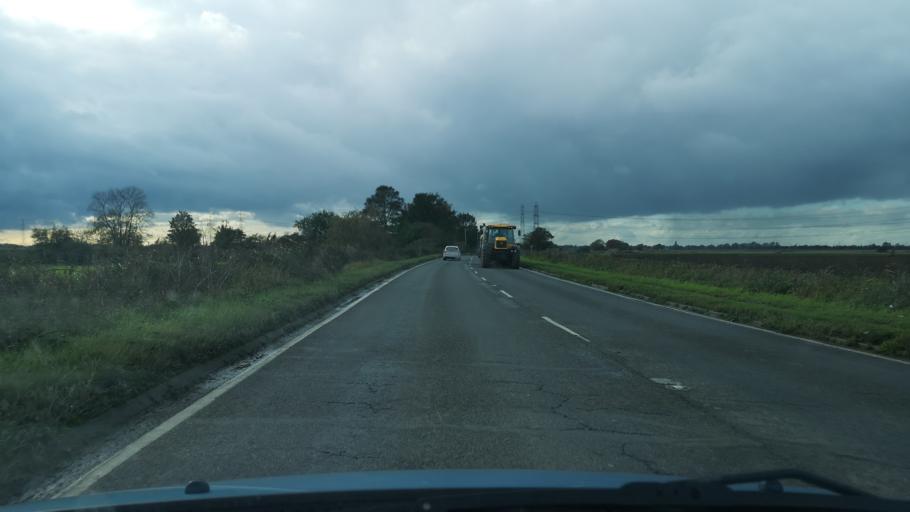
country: GB
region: England
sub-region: North Lincolnshire
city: Gunness
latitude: 53.5768
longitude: -0.7498
